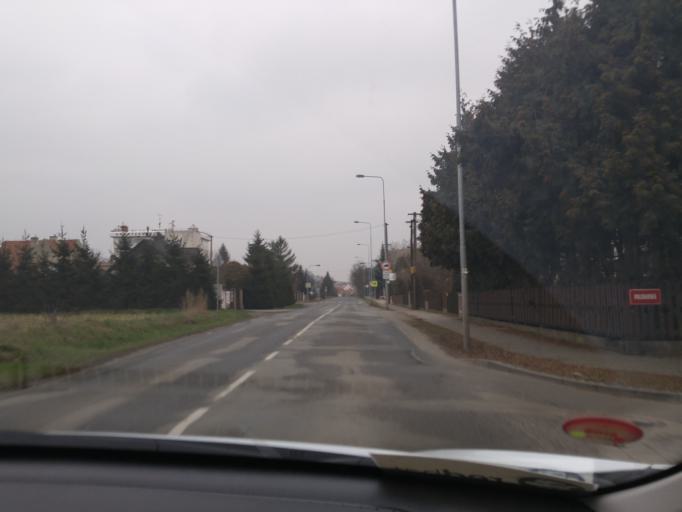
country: CZ
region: Central Bohemia
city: Brandys nad Labem-Stara Boleslav
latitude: 50.1906
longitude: 14.6483
